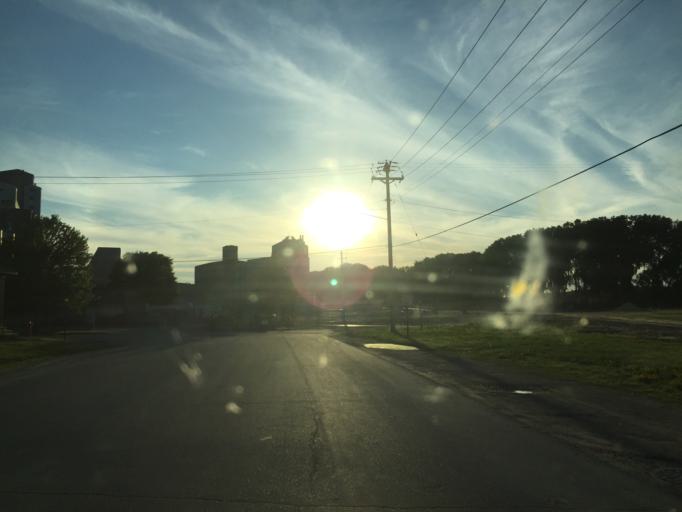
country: US
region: Minnesota
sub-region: Winona County
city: Winona
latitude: 44.0565
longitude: -91.6474
